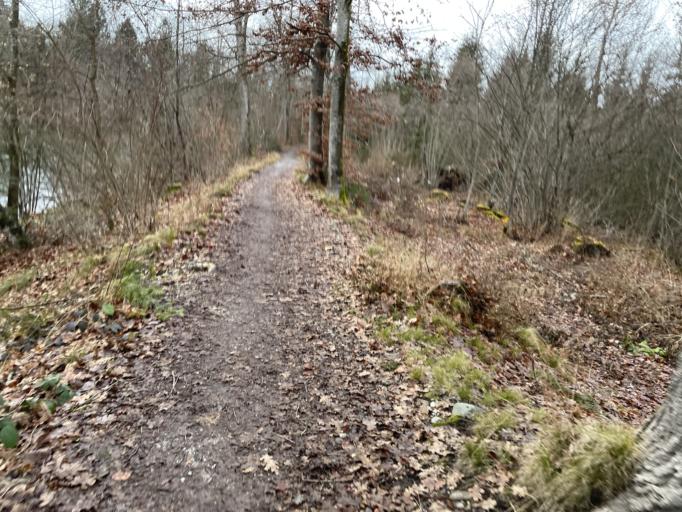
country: CH
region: Bern
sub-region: Thun District
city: Uttigen
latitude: 46.7991
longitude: 7.5740
